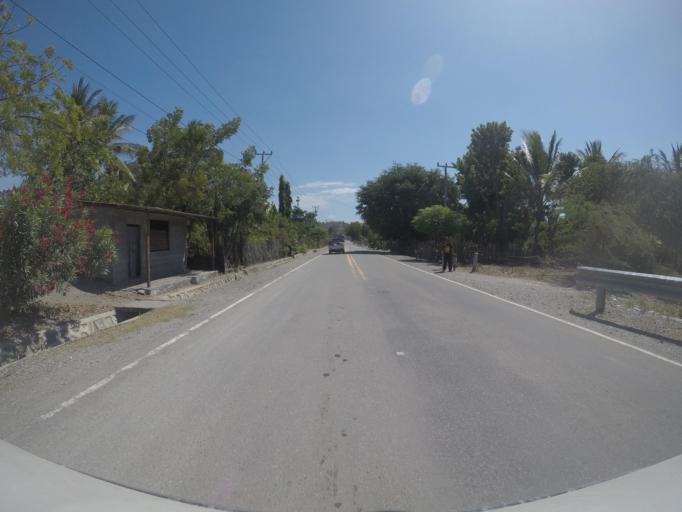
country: TL
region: Liquica
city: Liquica
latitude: -8.5687
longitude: 125.3845
